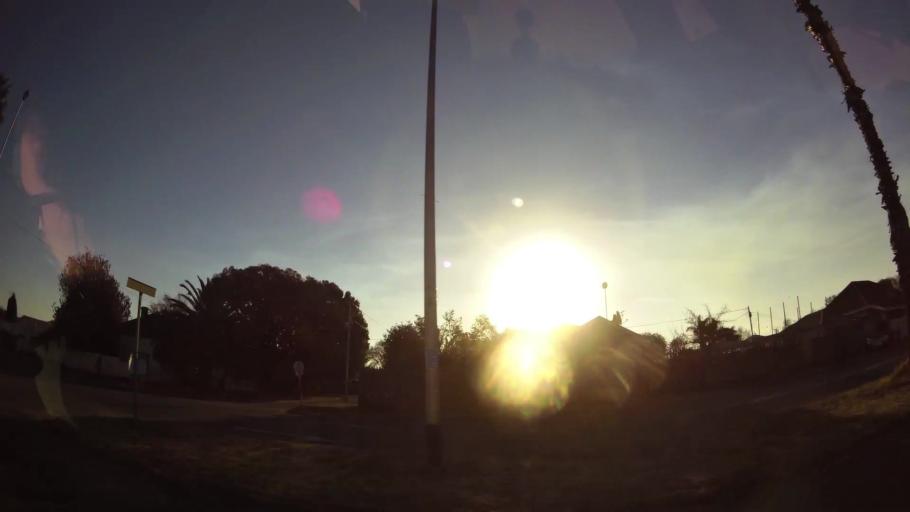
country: ZA
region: Gauteng
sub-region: City of Johannesburg Metropolitan Municipality
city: Roodepoort
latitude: -26.1604
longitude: 27.8738
